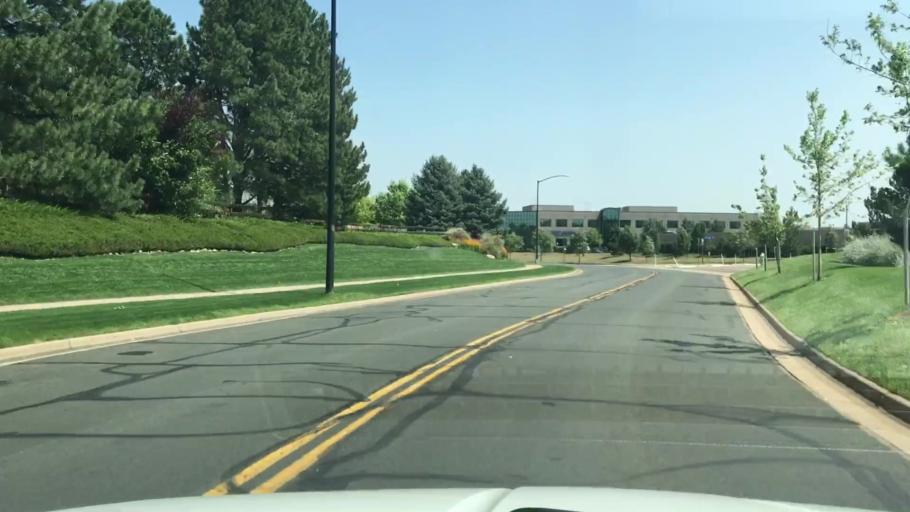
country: US
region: Colorado
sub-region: Boulder County
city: Gunbarrel
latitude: 40.0644
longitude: -105.2136
